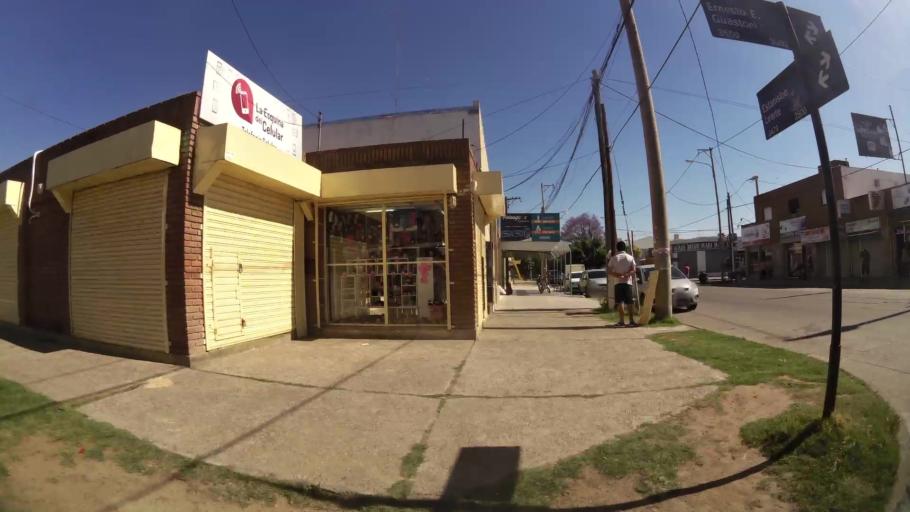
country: AR
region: Cordoba
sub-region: Departamento de Capital
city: Cordoba
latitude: -31.4393
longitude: -64.1392
